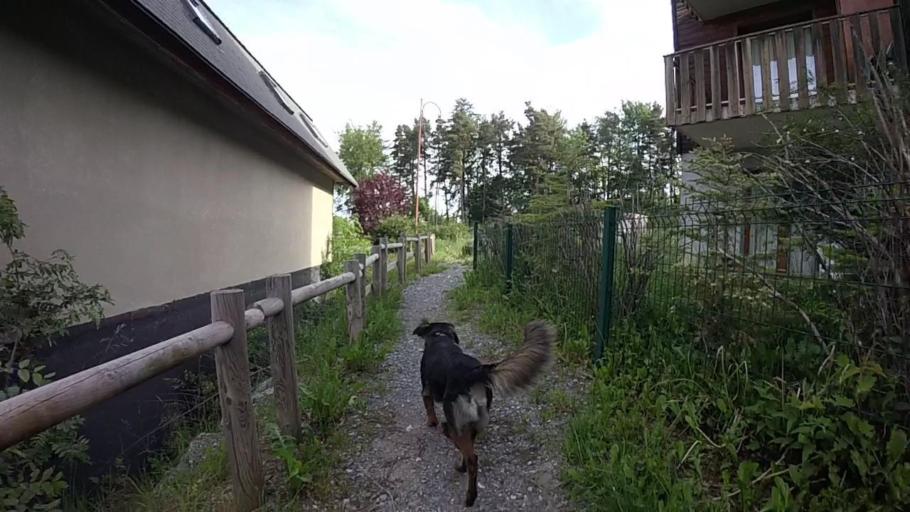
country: FR
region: Provence-Alpes-Cote d'Azur
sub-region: Departement des Alpes-de-Haute-Provence
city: Seyne-les-Alpes
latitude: 44.4130
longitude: 6.3521
